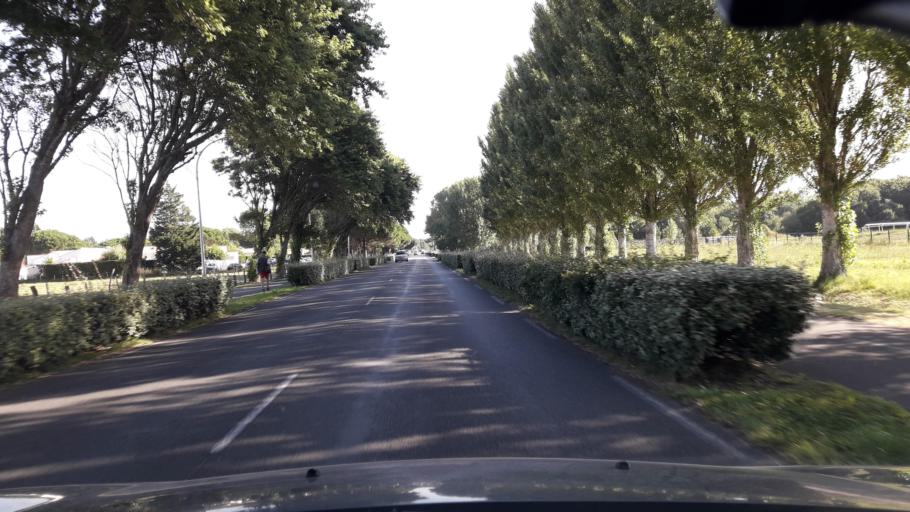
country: FR
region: Poitou-Charentes
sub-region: Departement de la Charente-Maritime
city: Les Mathes
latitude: 45.6978
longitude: -1.1735
